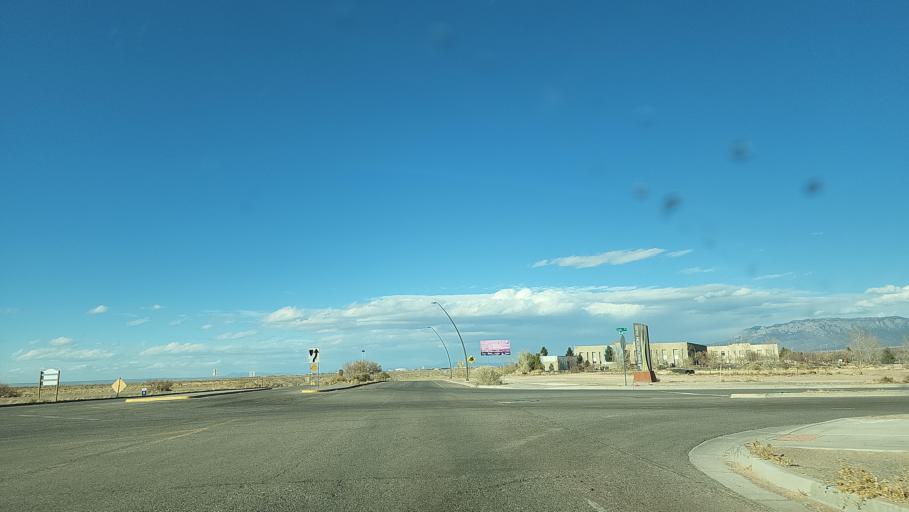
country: US
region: New Mexico
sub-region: Bernalillo County
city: South Valley
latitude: 35.0003
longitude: -106.6217
